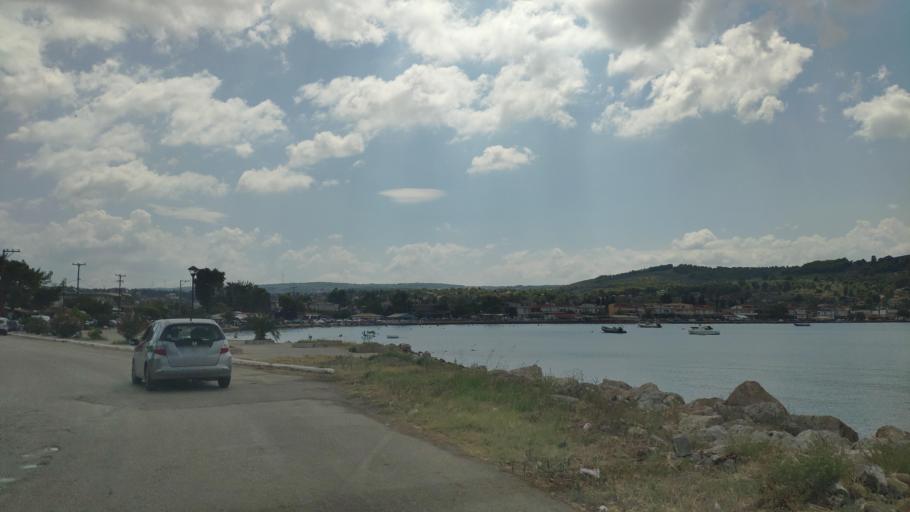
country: GR
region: Central Greece
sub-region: Nomos Fthiotidos
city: Malesina
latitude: 38.6575
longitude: 23.1901
